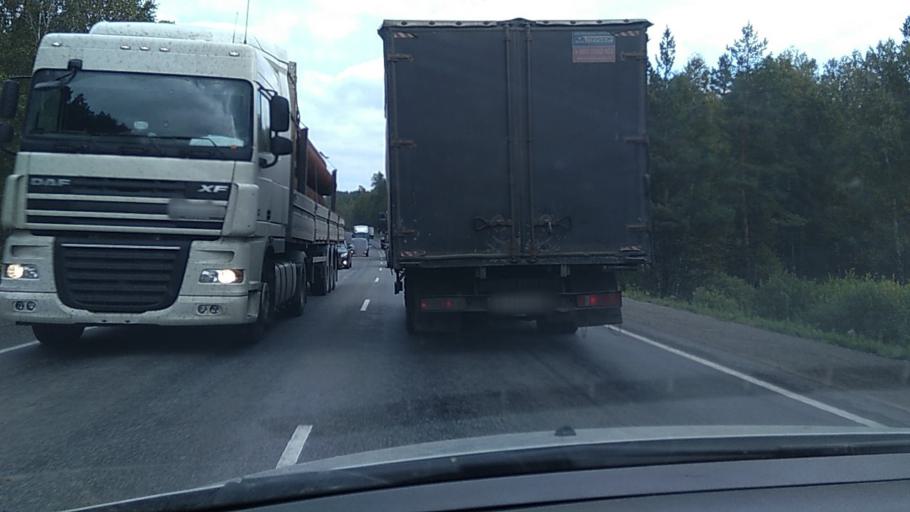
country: RU
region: Chelyabinsk
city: Miass
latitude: 54.9317
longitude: 60.1514
